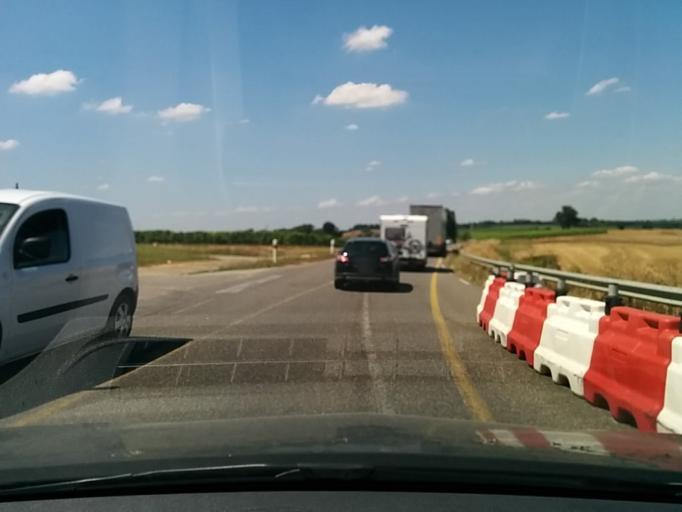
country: FR
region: Midi-Pyrenees
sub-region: Departement du Gers
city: Eauze
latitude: 43.7802
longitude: 0.1179
